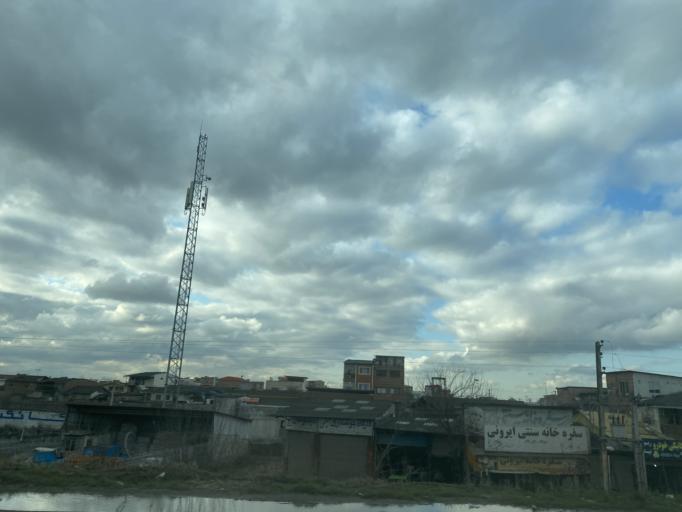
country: IR
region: Mazandaran
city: Amol
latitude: 36.4506
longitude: 52.3941
